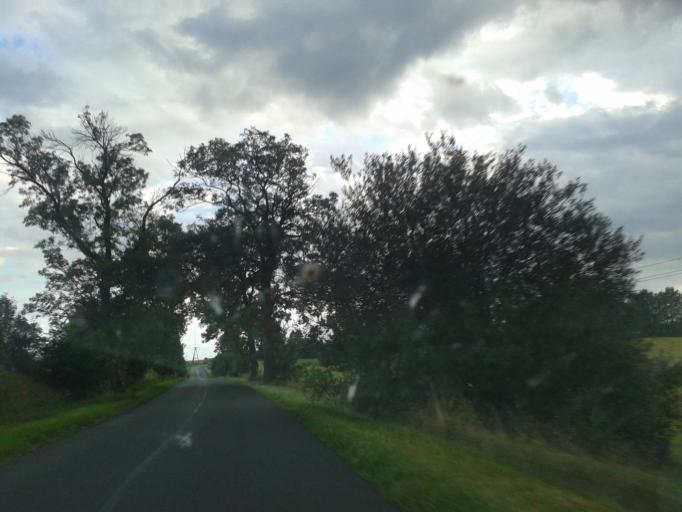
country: PL
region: West Pomeranian Voivodeship
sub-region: Powiat koszalinski
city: Bobolice
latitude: 53.8916
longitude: 16.5188
